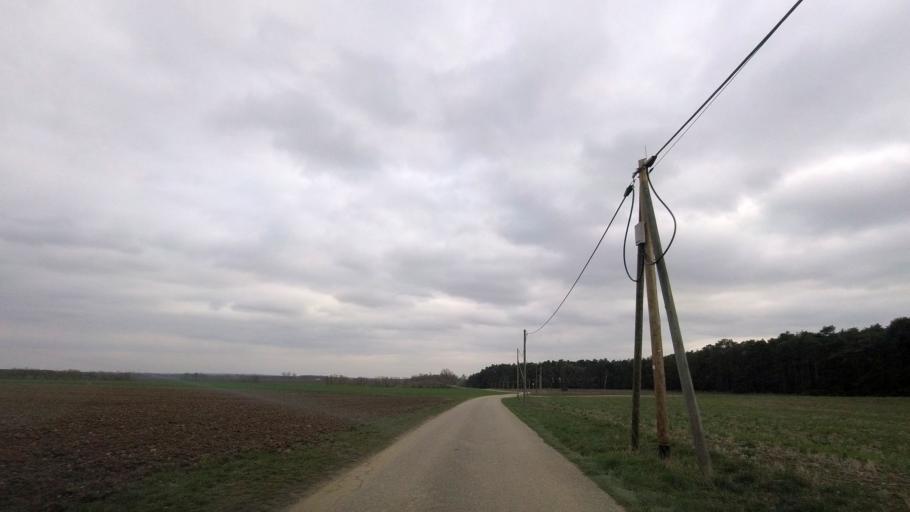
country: DE
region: Saxony-Anhalt
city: Seyda
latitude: 51.9095
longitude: 12.8878
